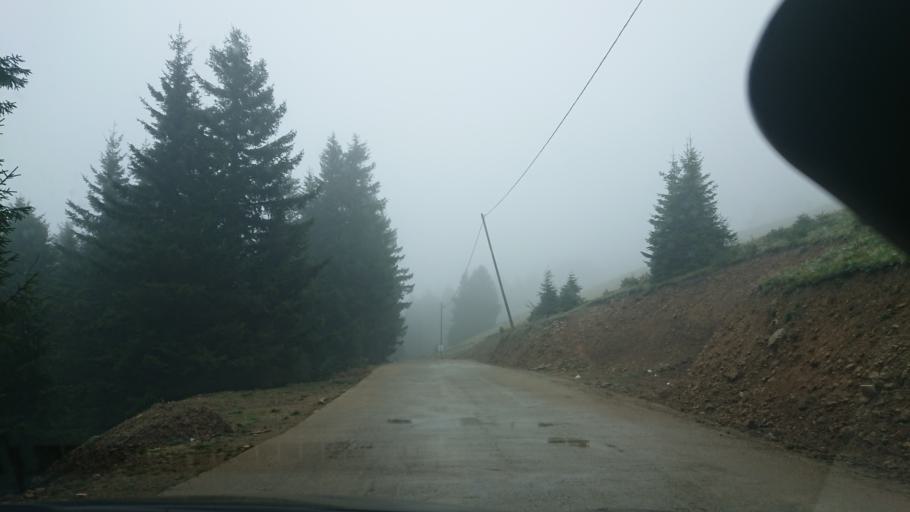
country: TR
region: Gumushane
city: Kurtun
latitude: 40.6706
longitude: 39.0045
